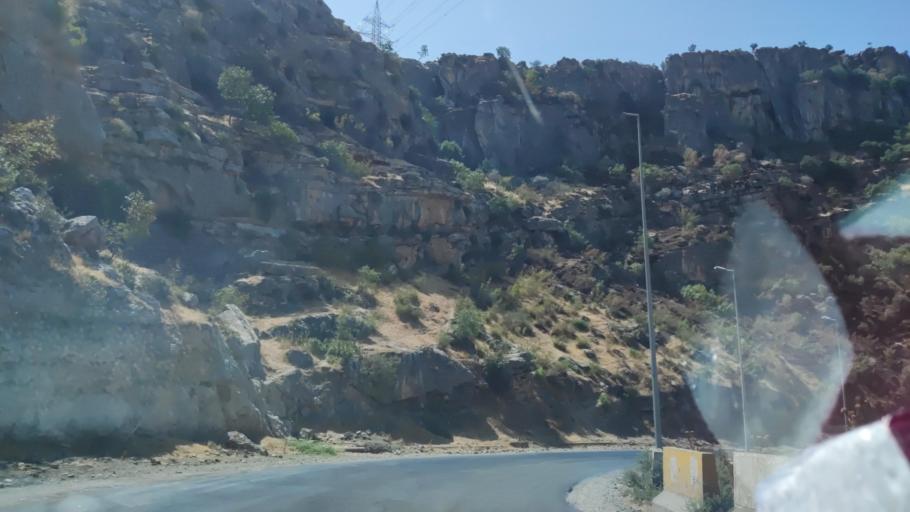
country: IQ
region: Arbil
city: Ruwandiz
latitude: 36.6460
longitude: 44.4968
